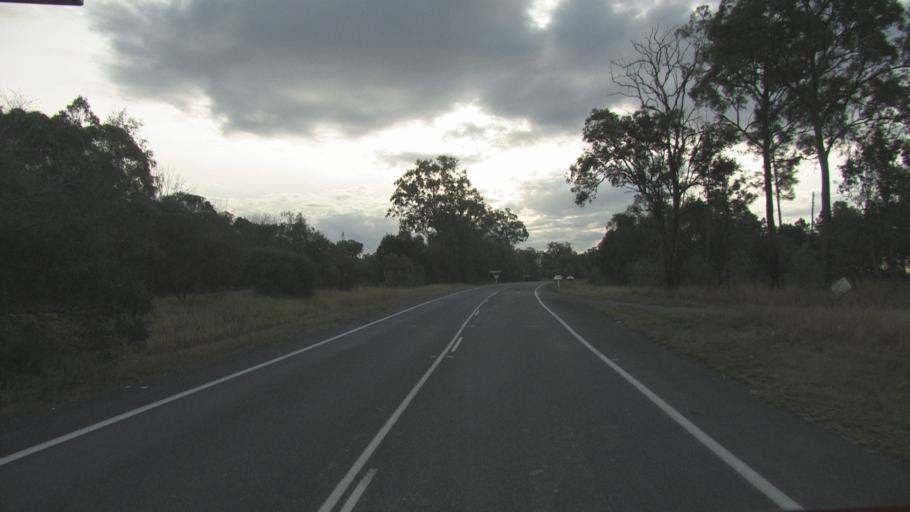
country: AU
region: Queensland
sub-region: Logan
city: Chambers Flat
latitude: -27.8377
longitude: 153.1097
